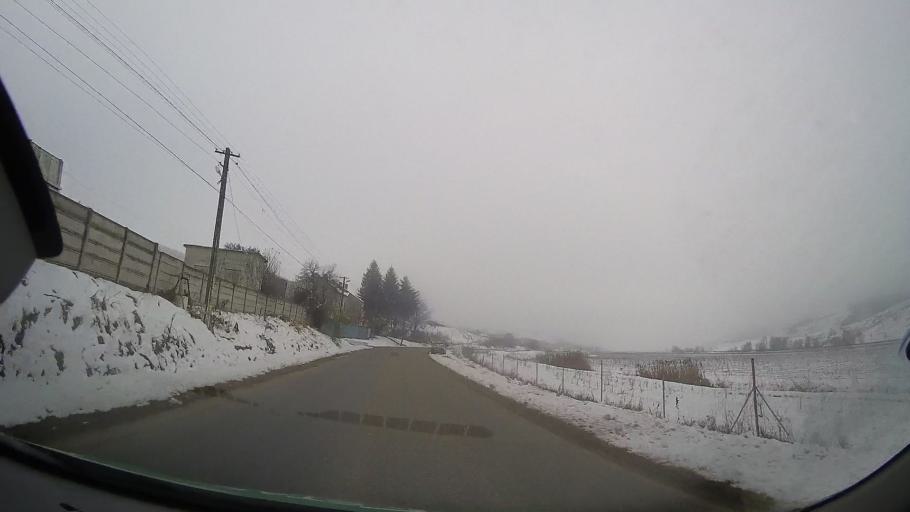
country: RO
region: Bacau
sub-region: Comuna Vultureni
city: Vultureni
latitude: 46.3668
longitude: 27.2846
